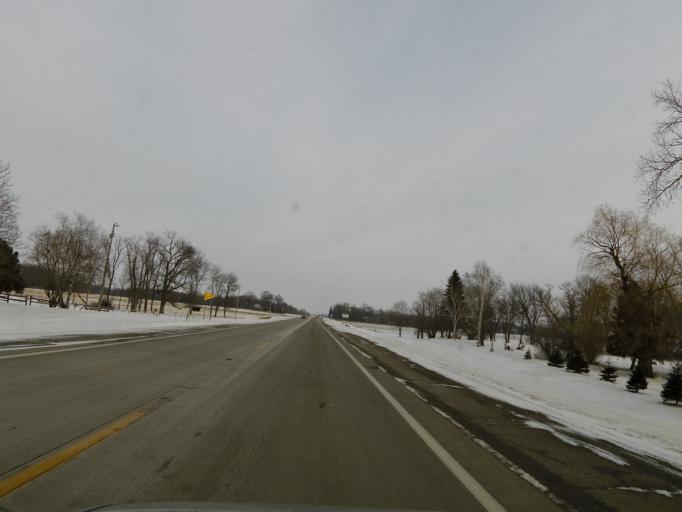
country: US
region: Minnesota
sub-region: McLeod County
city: Hutchinson
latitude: 44.8926
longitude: -94.2841
